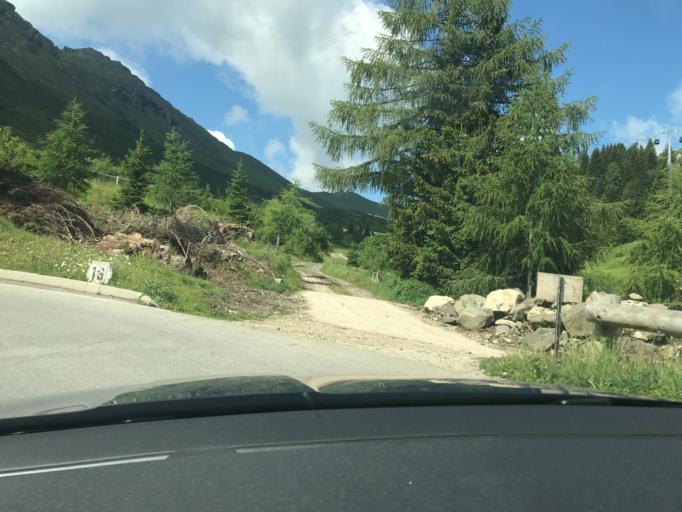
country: IT
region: Trentino-Alto Adige
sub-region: Bolzano
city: Corvara in Badia
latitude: 46.4877
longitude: 11.8438
